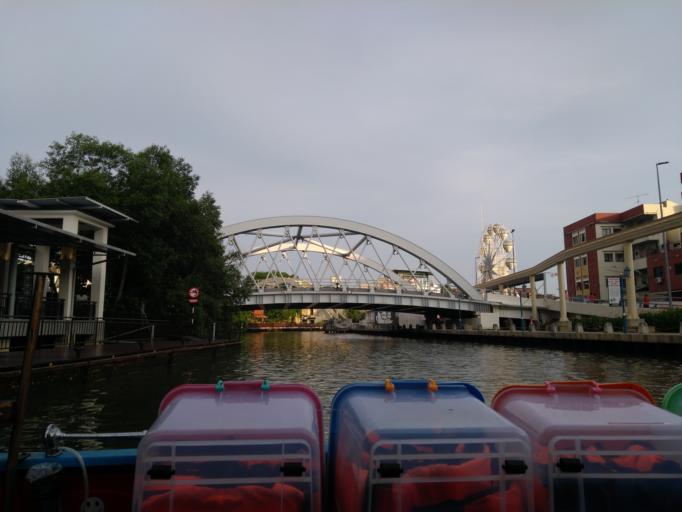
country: MY
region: Melaka
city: Malacca
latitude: 2.2021
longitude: 102.2493
